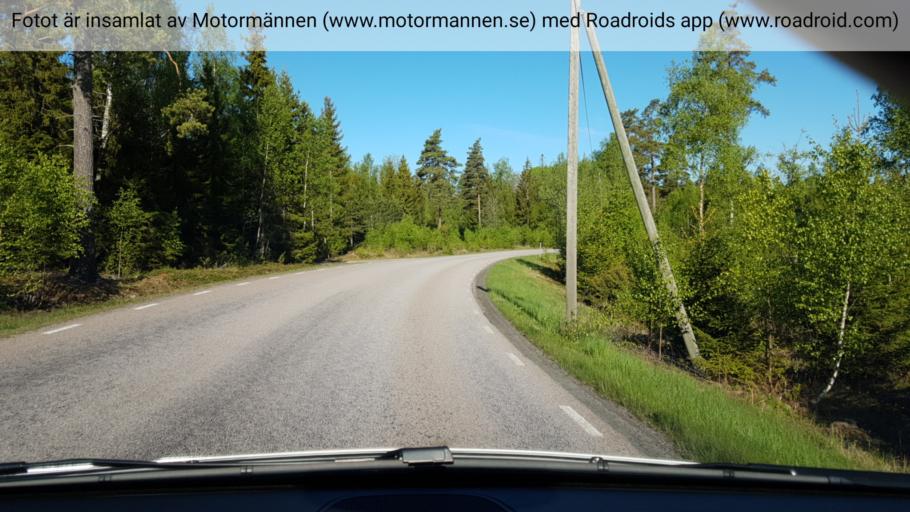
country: SE
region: Vaestra Goetaland
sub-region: Skovde Kommun
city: Stopen
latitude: 58.5391
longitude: 13.6975
